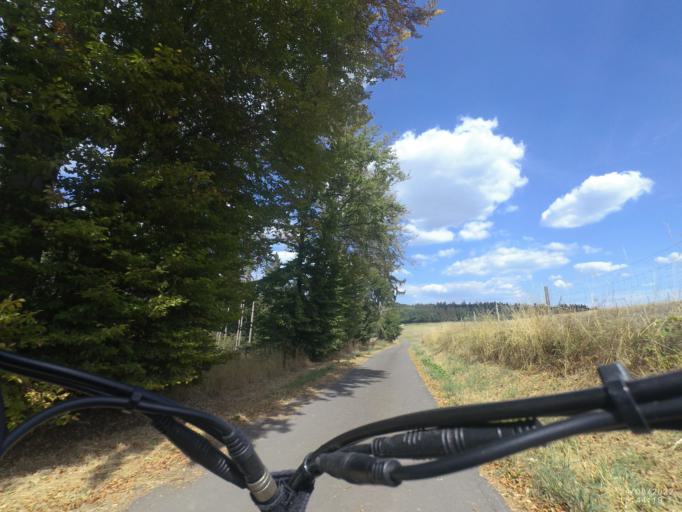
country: DE
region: Rheinland-Pfalz
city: Neroth
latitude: 50.2049
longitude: 6.7461
